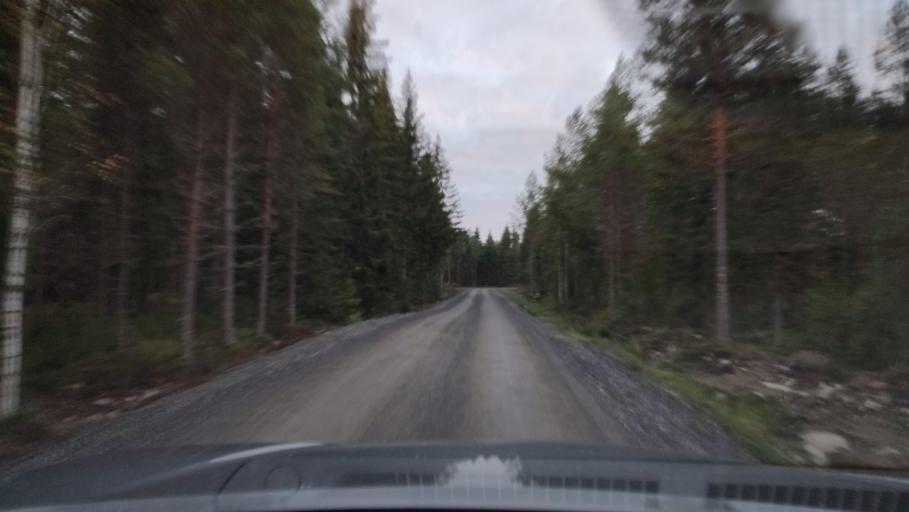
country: FI
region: Southern Ostrobothnia
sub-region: Suupohja
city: Karijoki
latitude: 62.1933
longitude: 21.5754
